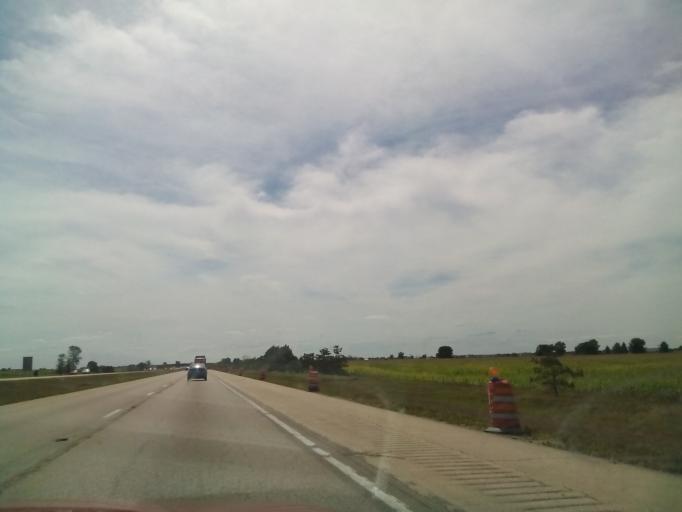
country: US
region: Illinois
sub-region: Ogle County
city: Davis Junction
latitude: 42.0894
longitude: -89.0229
